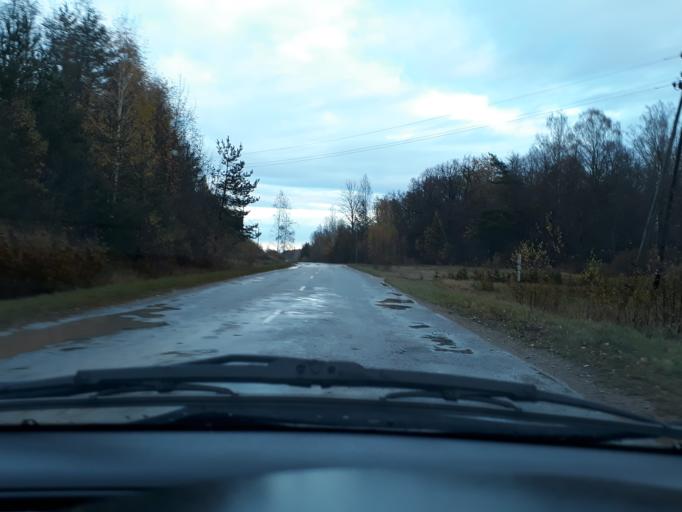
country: LV
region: Dobeles Rajons
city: Dobele
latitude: 56.6073
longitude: 23.2232
